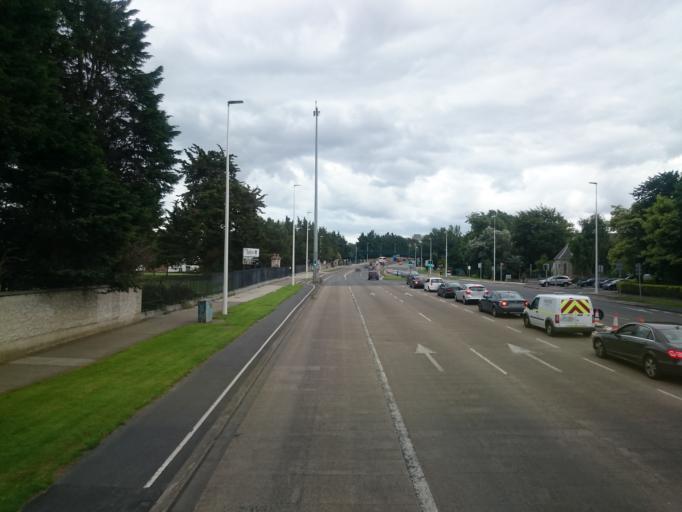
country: IE
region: Leinster
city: Mount Merrion
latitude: 53.3042
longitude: -6.2092
